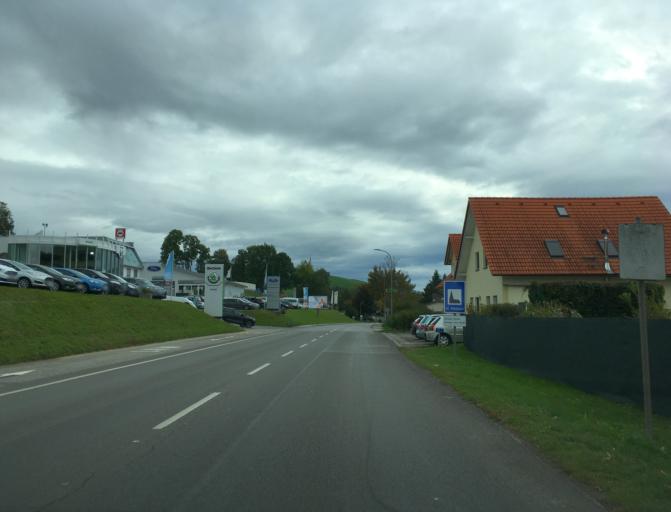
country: AT
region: Lower Austria
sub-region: Politischer Bezirk Wiener Neustadt
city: Bad Schonau
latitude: 47.5270
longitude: 16.1859
